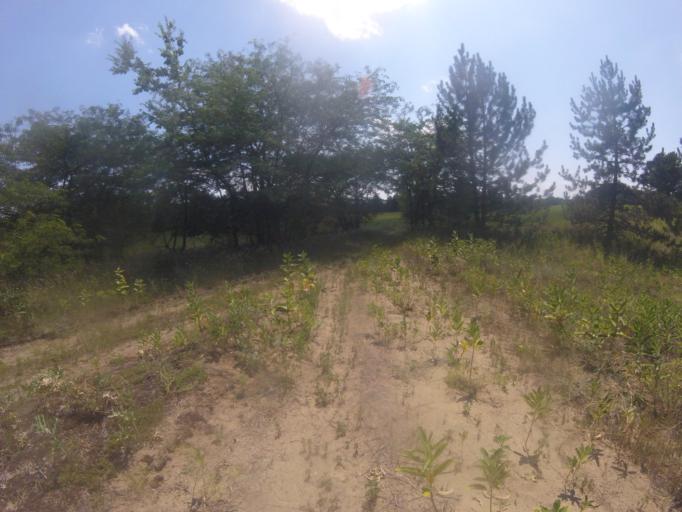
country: HU
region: Bacs-Kiskun
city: Jaszszentlaszlo
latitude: 46.6077
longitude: 19.7146
